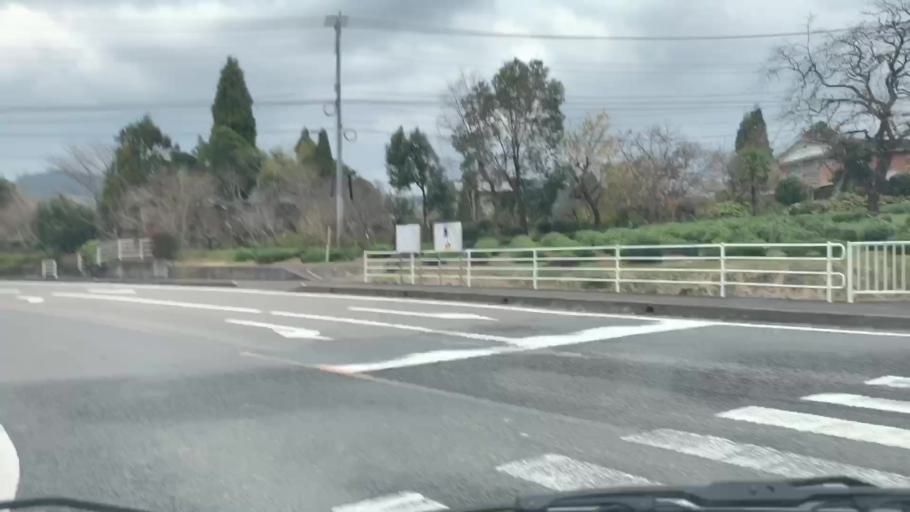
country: JP
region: Saga Prefecture
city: Ureshinomachi-shimojuku
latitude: 33.1366
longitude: 129.9881
